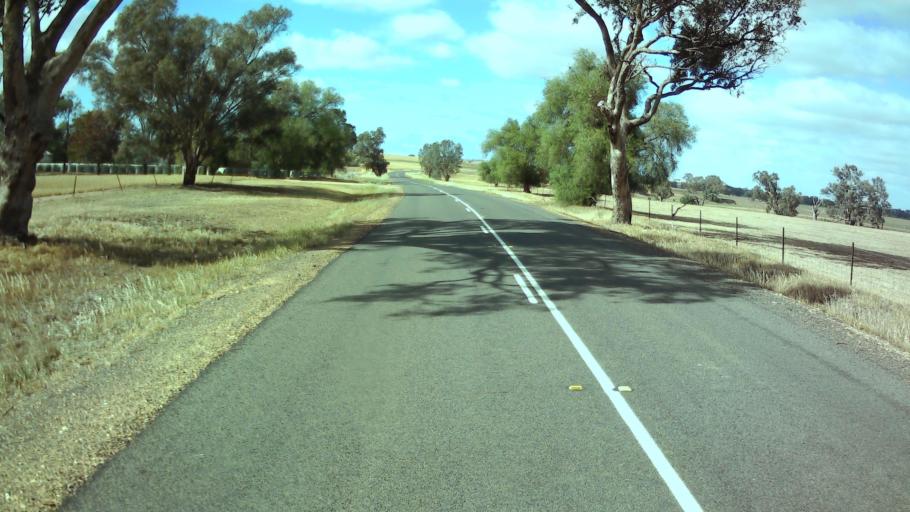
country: AU
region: New South Wales
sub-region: Weddin
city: Grenfell
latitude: -33.9716
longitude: 148.4261
